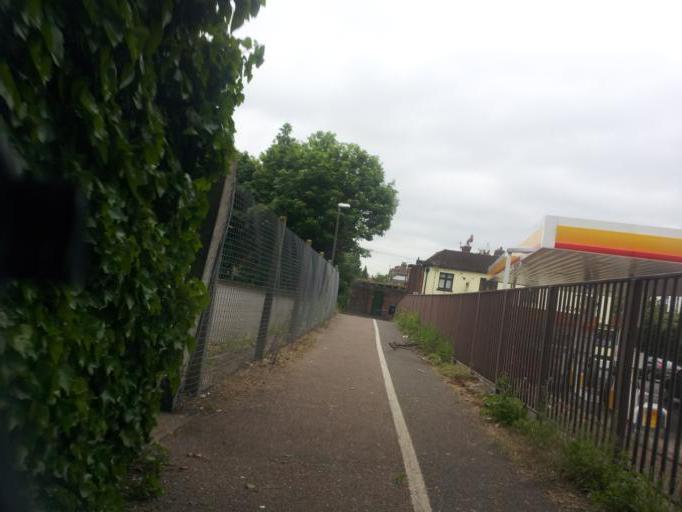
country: GB
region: England
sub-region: Kent
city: Maidstone
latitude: 51.2831
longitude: 0.5186
